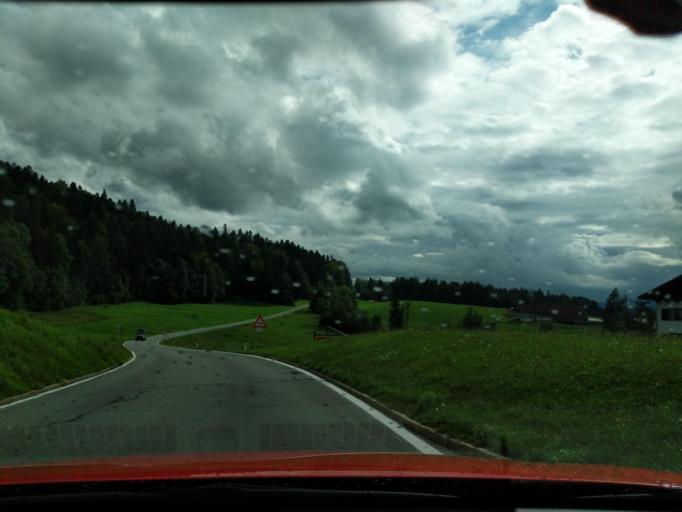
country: AT
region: Vorarlberg
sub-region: Politischer Bezirk Bregenz
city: Riefensberg
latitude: 47.5109
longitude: 9.9522
